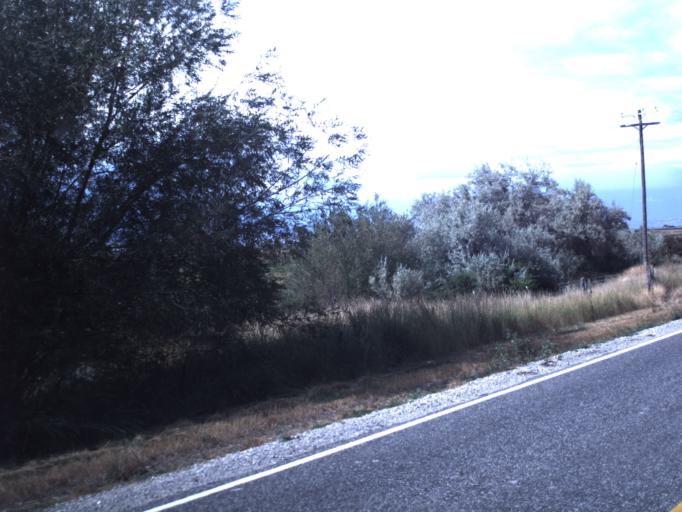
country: US
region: Utah
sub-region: Cache County
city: Lewiston
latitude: 41.9180
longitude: -111.9105
